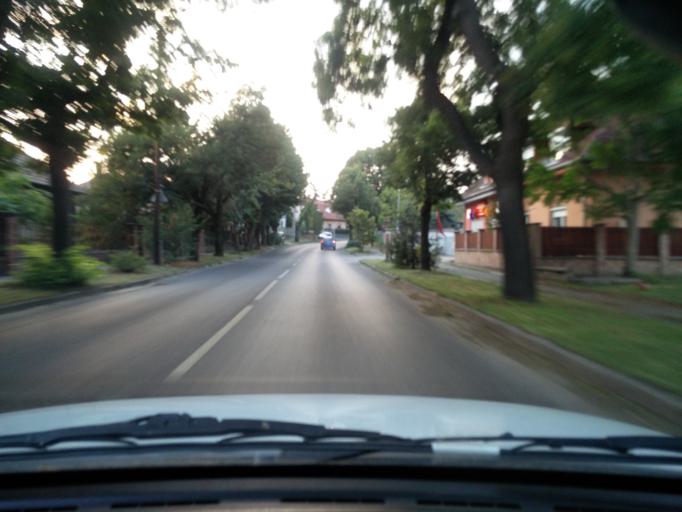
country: HU
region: Budapest
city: Budapest XXIII. keruelet
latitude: 47.4015
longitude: 19.0939
